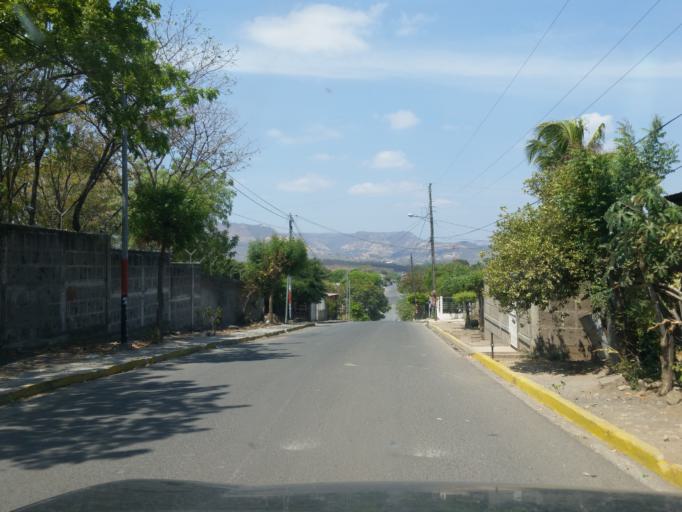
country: NI
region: Matagalpa
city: Ciudad Dario
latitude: 12.7297
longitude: -86.1193
